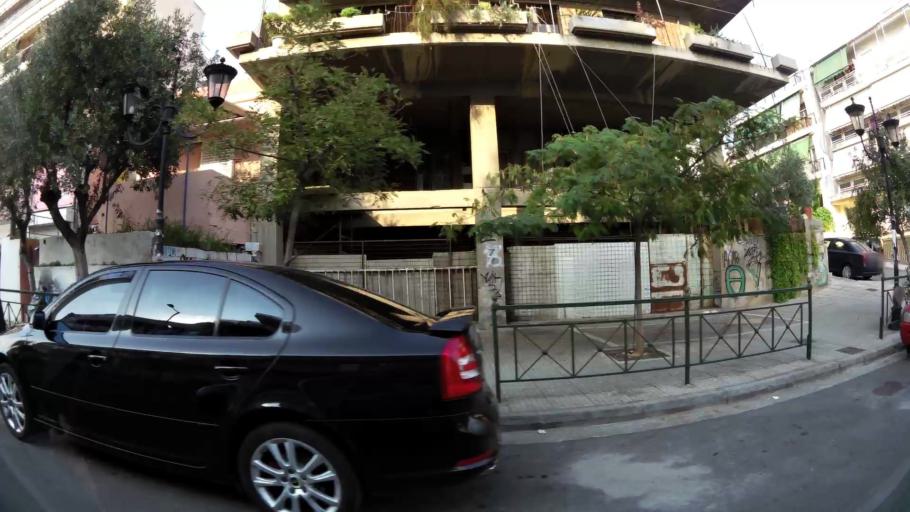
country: GR
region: Attica
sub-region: Nomarchia Athinas
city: Petroupolis
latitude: 38.0440
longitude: 23.6806
